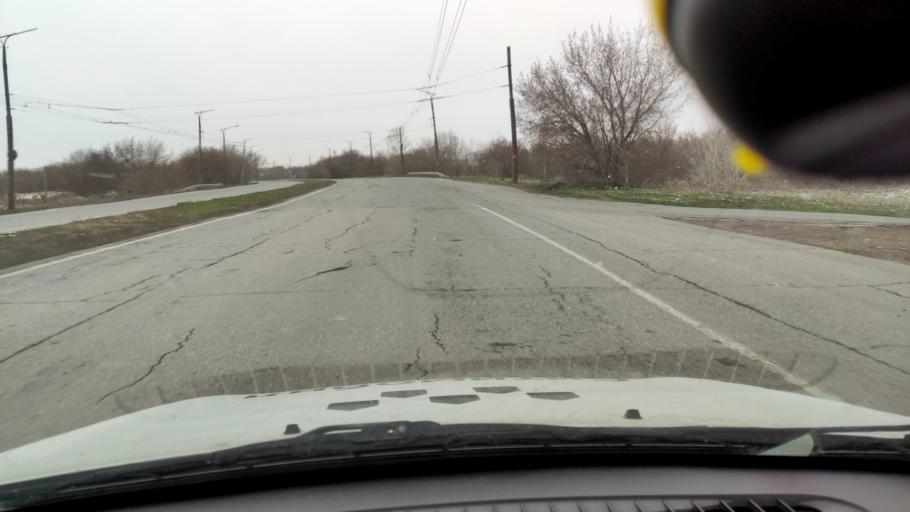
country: RU
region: Samara
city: Zhigulevsk
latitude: 53.5414
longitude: 49.5730
